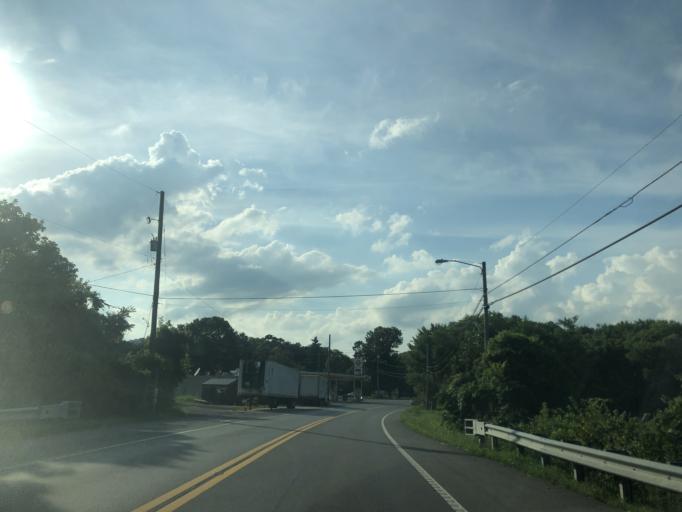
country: US
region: Tennessee
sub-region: Davidson County
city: Nashville
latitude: 36.2512
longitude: -86.8287
